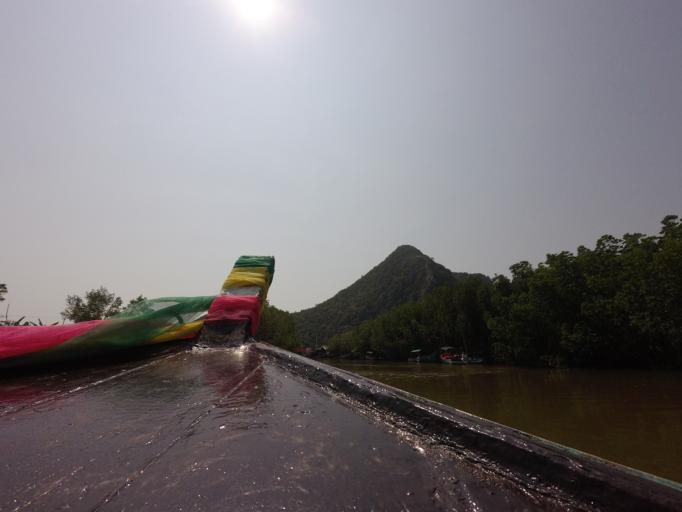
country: TH
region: Prachuap Khiri Khan
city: Kui Buri
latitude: 12.1365
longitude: 99.9614
